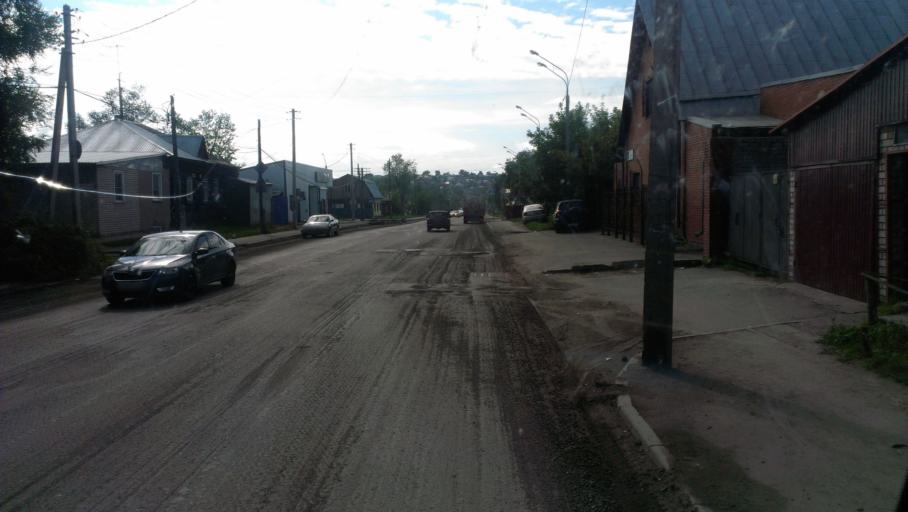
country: RU
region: Altai Krai
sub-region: Gorod Barnaulskiy
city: Barnaul
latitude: 53.3268
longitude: 83.7637
